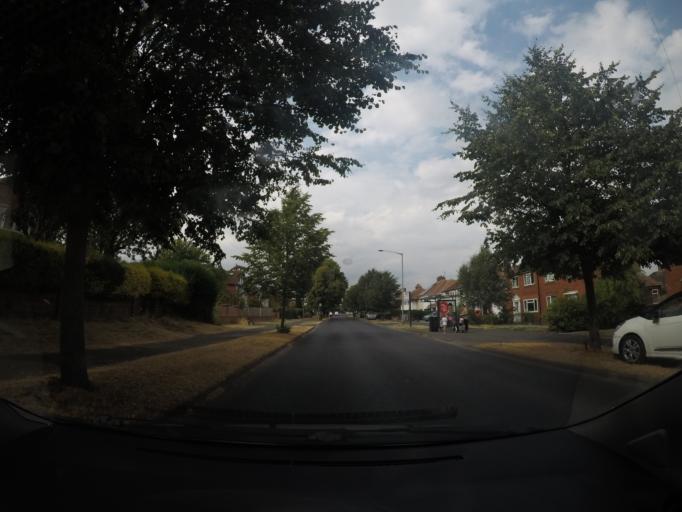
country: GB
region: England
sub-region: City of York
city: Nether Poppleton
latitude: 53.9609
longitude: -1.1350
